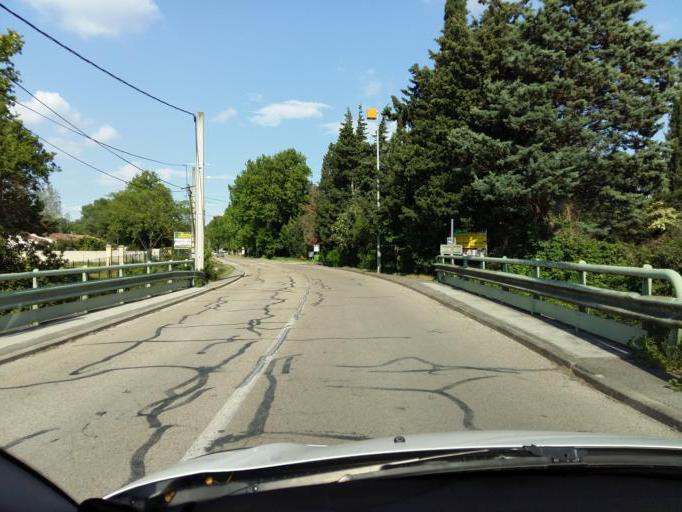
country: FR
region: Provence-Alpes-Cote d'Azur
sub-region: Departement des Bouches-du-Rhone
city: Noves
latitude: 43.8788
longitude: 4.9064
